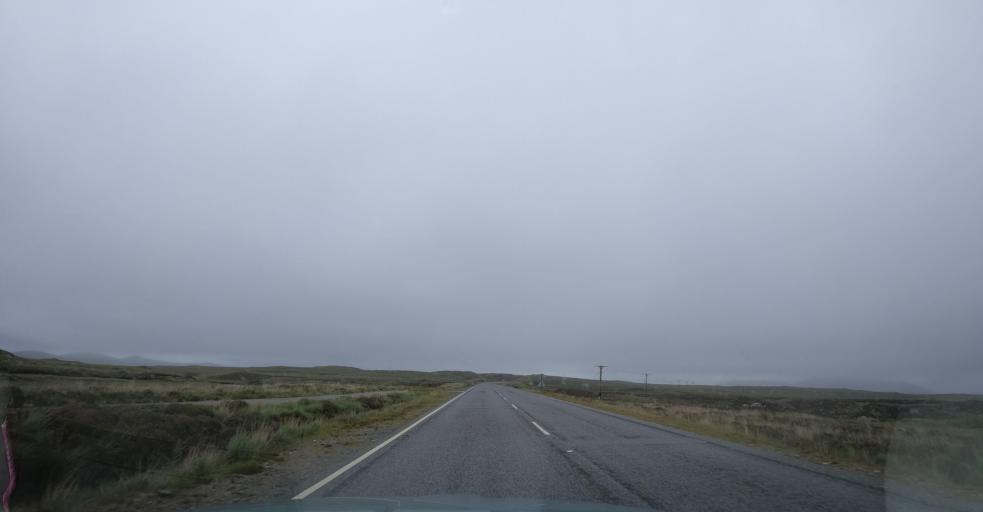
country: GB
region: Scotland
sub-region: Eilean Siar
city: Isle of North Uist
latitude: 57.5764
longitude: -7.2627
